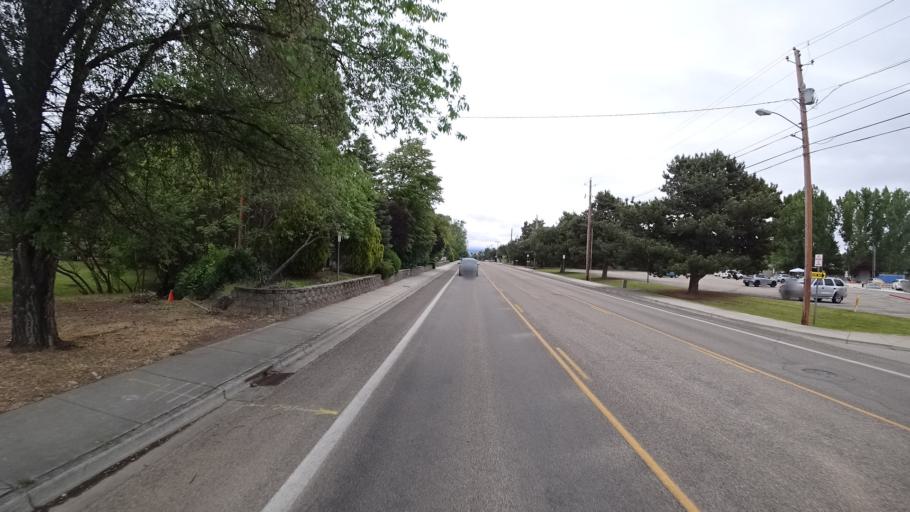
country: US
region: Idaho
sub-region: Ada County
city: Eagle
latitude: 43.6485
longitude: -116.3180
